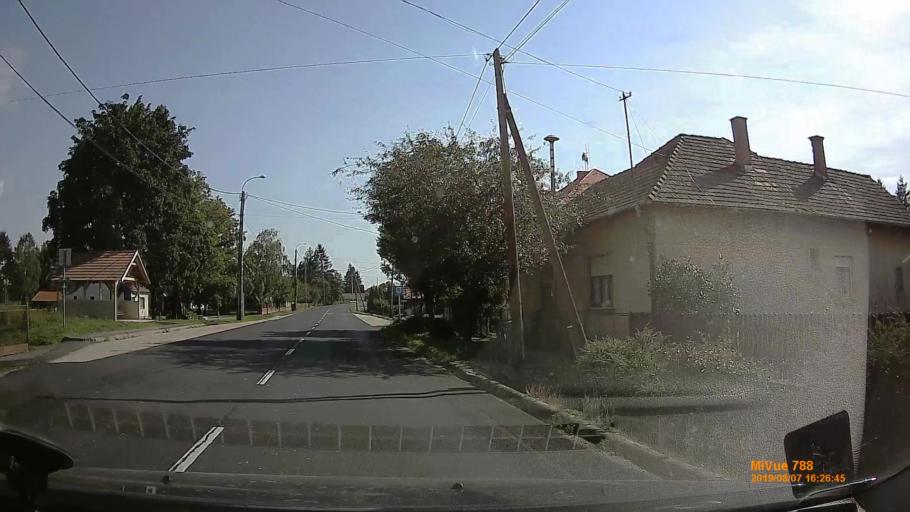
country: HU
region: Zala
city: Lenti
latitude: 46.7073
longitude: 16.5520
